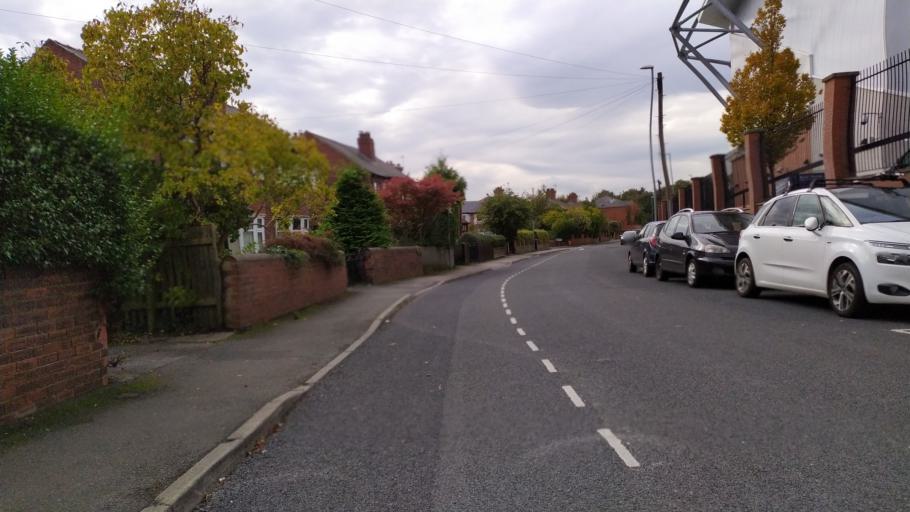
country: GB
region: England
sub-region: City and Borough of Leeds
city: Leeds
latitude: 53.8160
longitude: -1.5809
